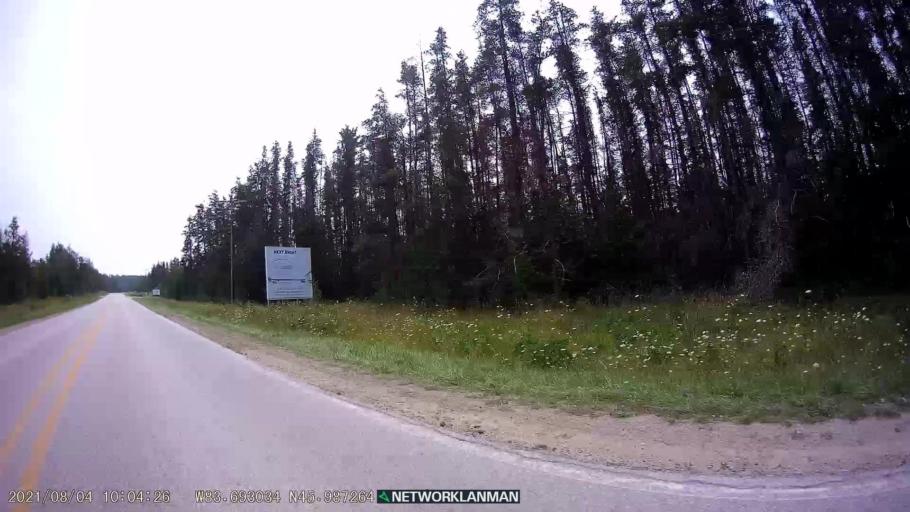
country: CA
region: Ontario
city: Thessalon
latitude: 45.9873
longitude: -83.6931
